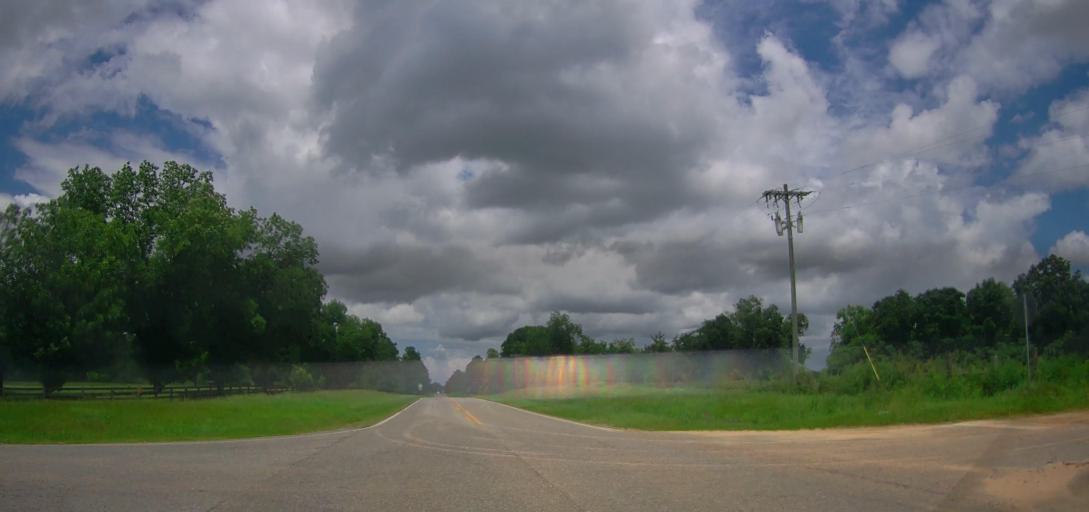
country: US
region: Georgia
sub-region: Wilcox County
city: Rochelle
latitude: 31.8991
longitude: -83.5531
